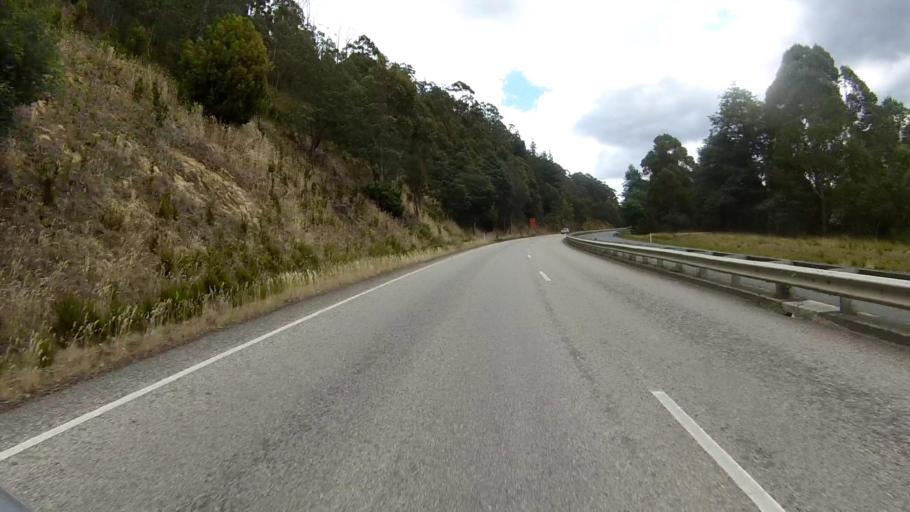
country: AU
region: Tasmania
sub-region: Kingborough
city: Margate
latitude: -42.9849
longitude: 147.1803
